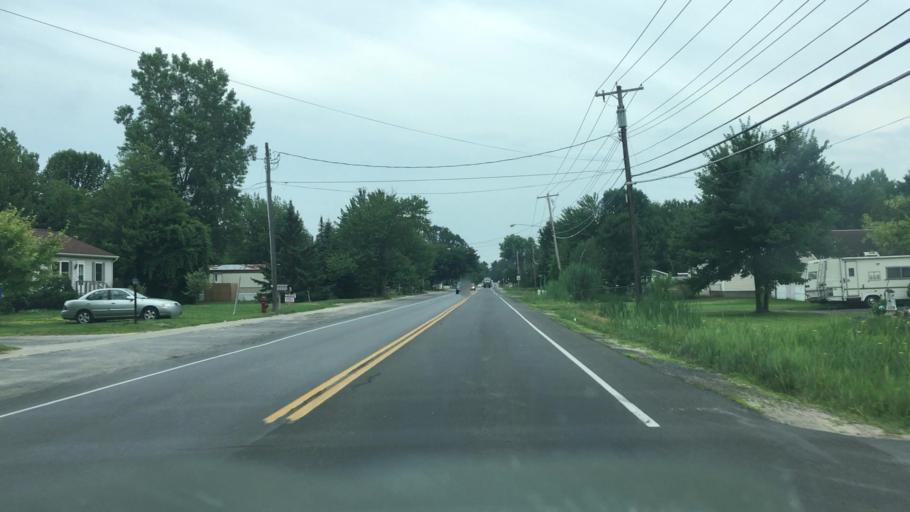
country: US
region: New York
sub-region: Clinton County
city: Plattsburgh West
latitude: 44.6831
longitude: -73.5067
